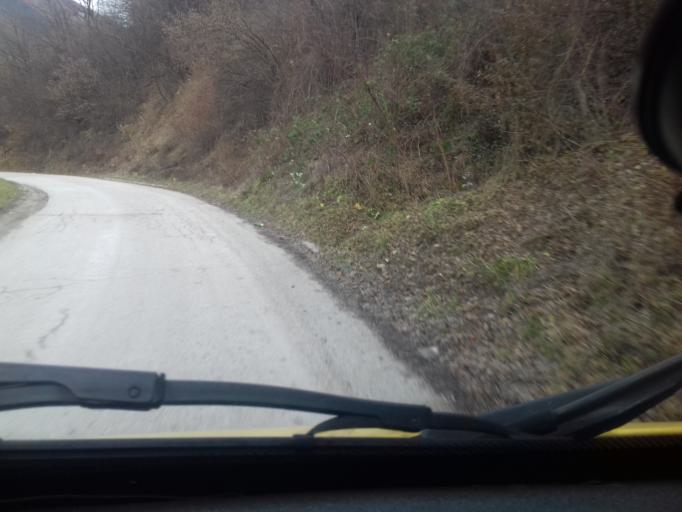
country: BA
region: Federation of Bosnia and Herzegovina
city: Zenica
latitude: 44.2433
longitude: 17.9182
